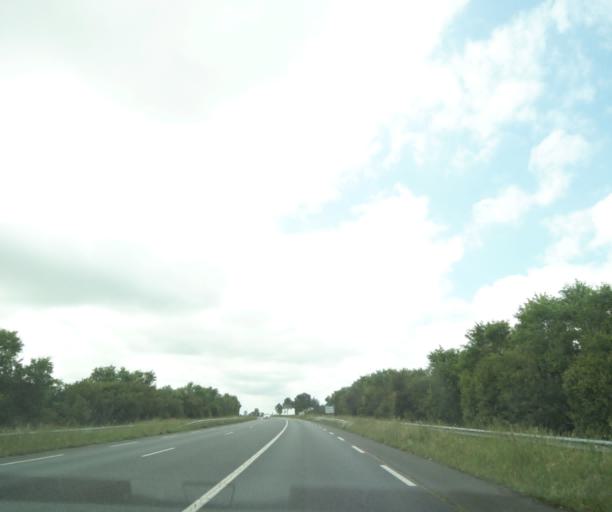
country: FR
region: Poitou-Charentes
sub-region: Departement des Deux-Sevres
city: Viennay
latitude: 46.7776
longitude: -0.2188
